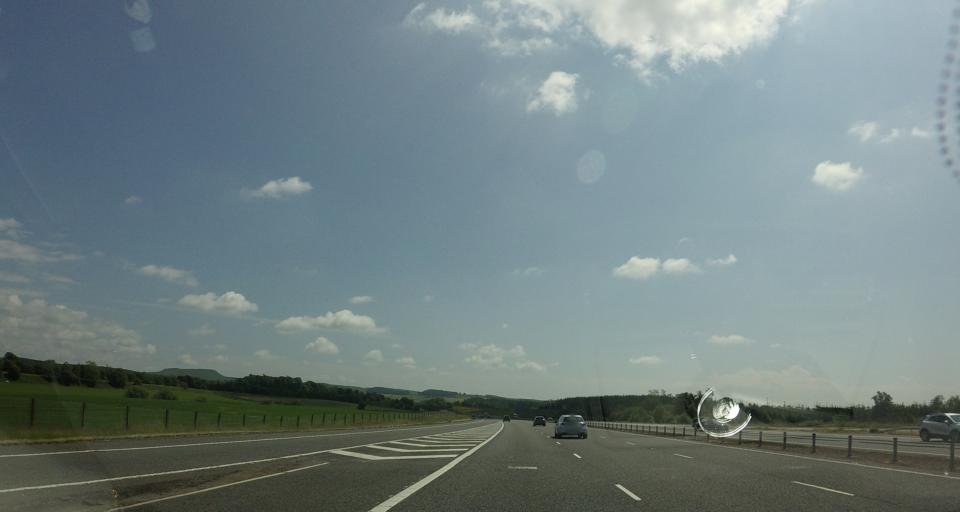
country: GB
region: Scotland
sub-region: Dumfries and Galloway
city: Lockerbie
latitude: 55.1024
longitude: -3.3462
